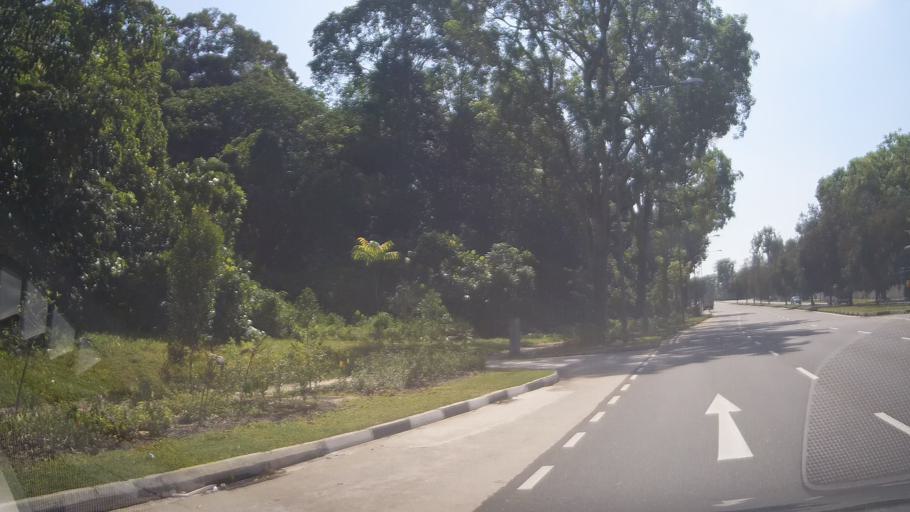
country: MY
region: Johor
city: Johor Bahru
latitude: 1.4103
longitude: 103.7660
